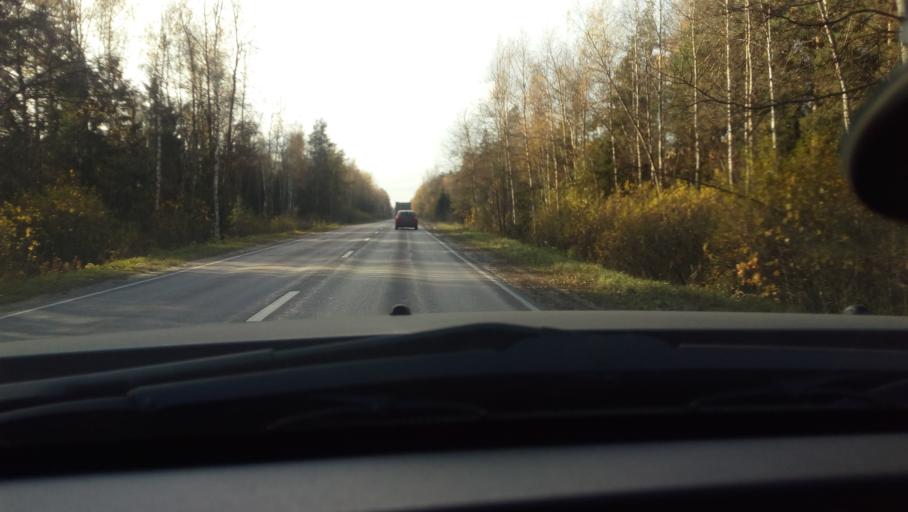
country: RU
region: Moskovskaya
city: Fryazevo
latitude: 55.7053
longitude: 38.4478
